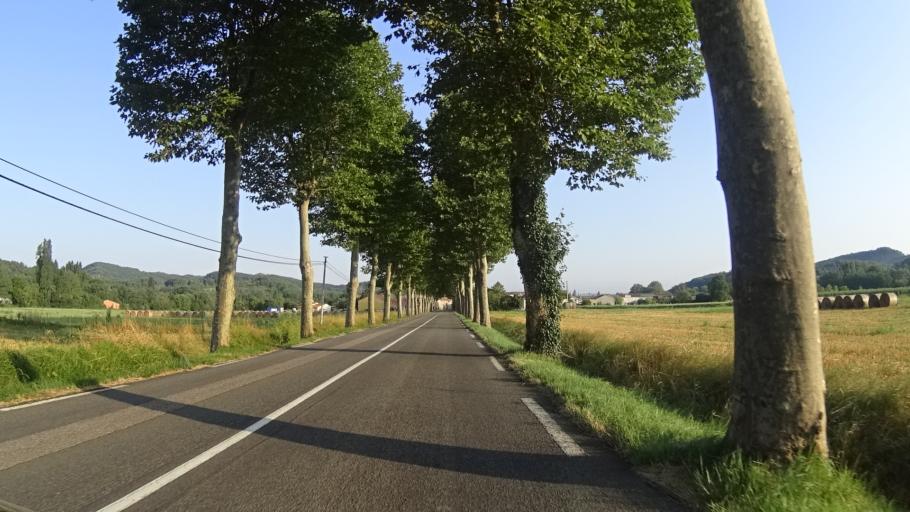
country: FR
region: Midi-Pyrenees
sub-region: Departement de l'Ariege
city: Mirepoix
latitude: 43.0504
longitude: 1.8897
